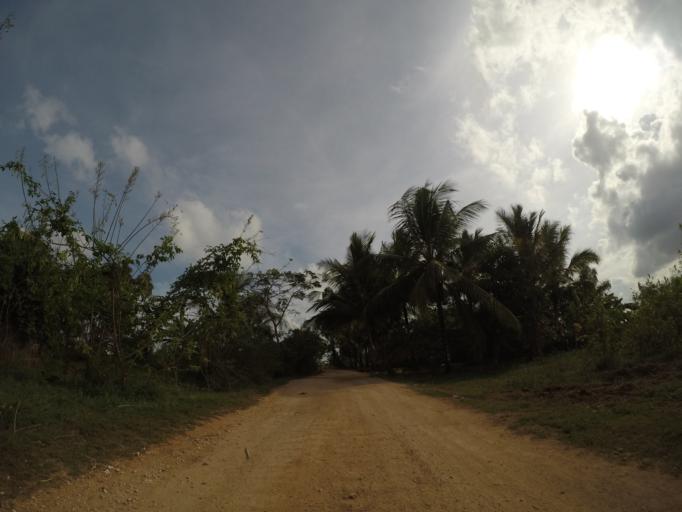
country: TZ
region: Zanzibar Central/South
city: Koani
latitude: -6.2296
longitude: 39.3192
